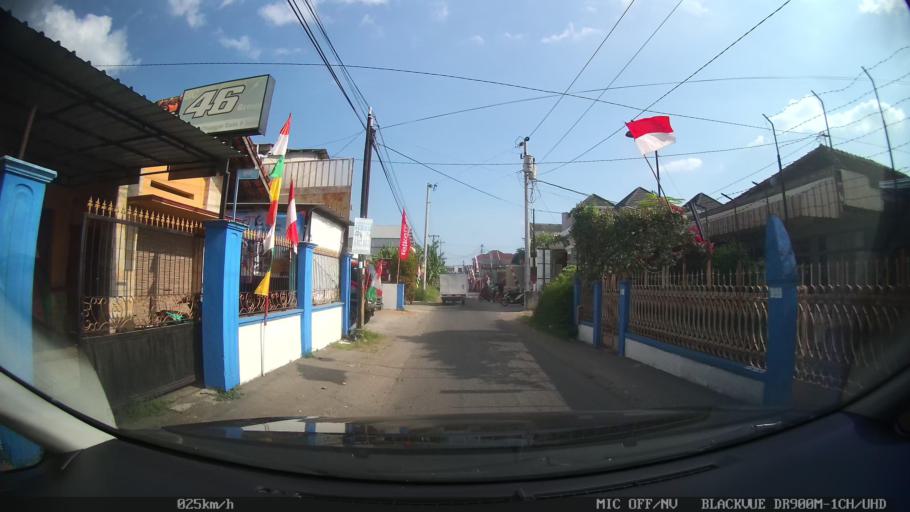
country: ID
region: Daerah Istimewa Yogyakarta
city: Gamping Lor
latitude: -7.7985
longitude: 110.3416
